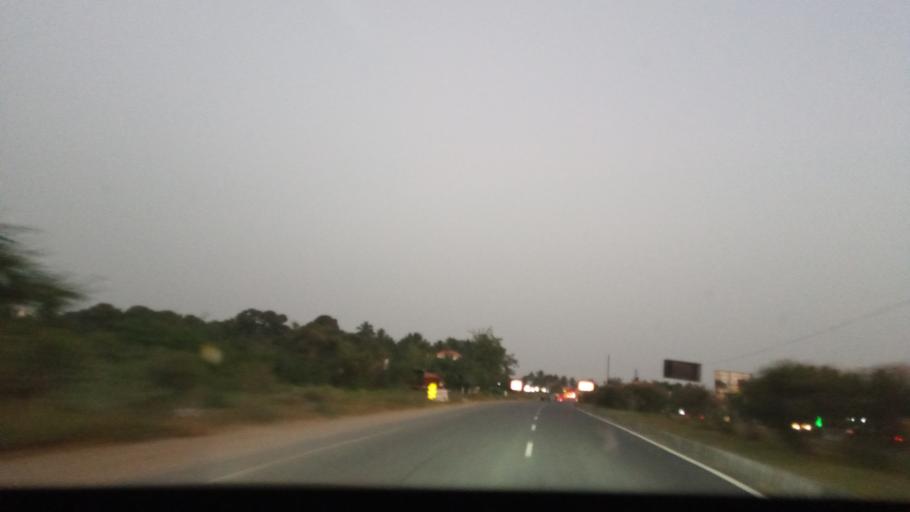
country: IN
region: Tamil Nadu
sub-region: Salem
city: Attur
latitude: 11.6156
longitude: 78.5618
